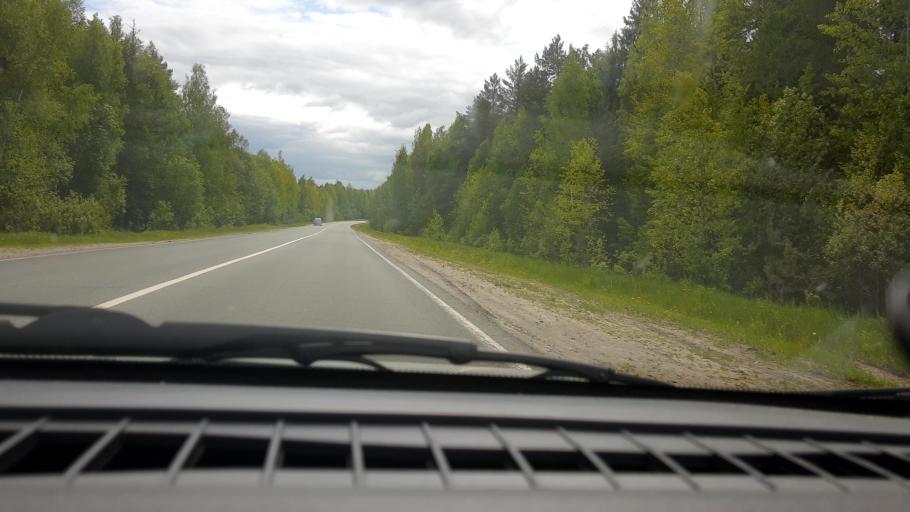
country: RU
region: Nizjnij Novgorod
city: Semenov
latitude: 56.7999
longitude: 44.4603
